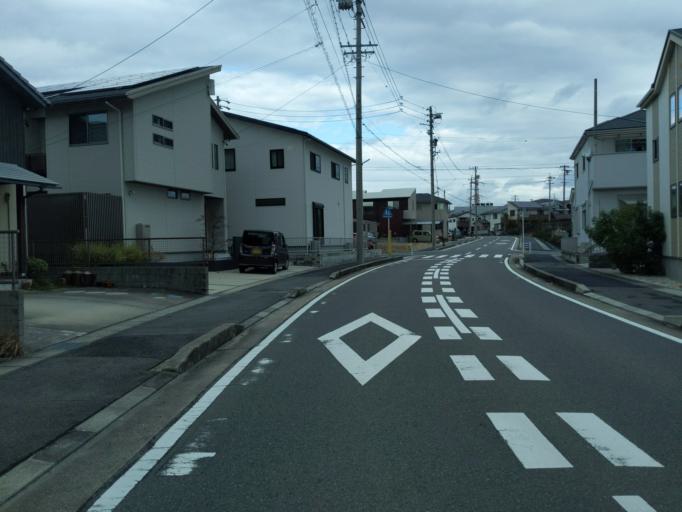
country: JP
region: Aichi
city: Kasugai
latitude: 35.2590
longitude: 136.9918
